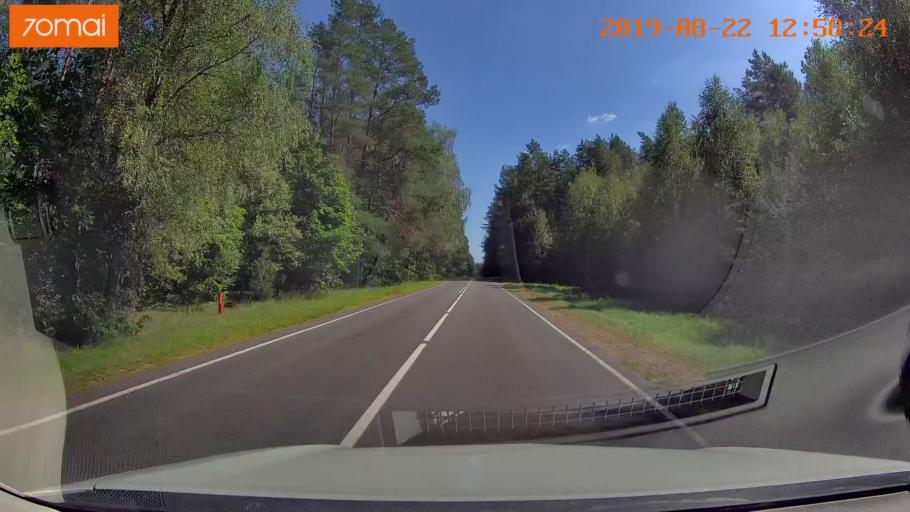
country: BY
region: Minsk
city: Prawdzinski
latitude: 53.4242
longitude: 27.7699
